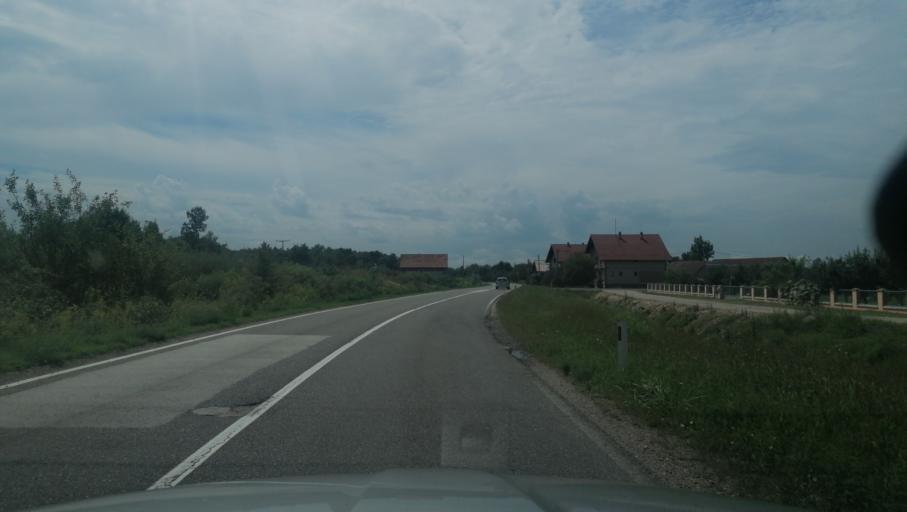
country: BA
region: Republika Srpska
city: Bosanski Samac
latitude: 45.0141
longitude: 18.5170
